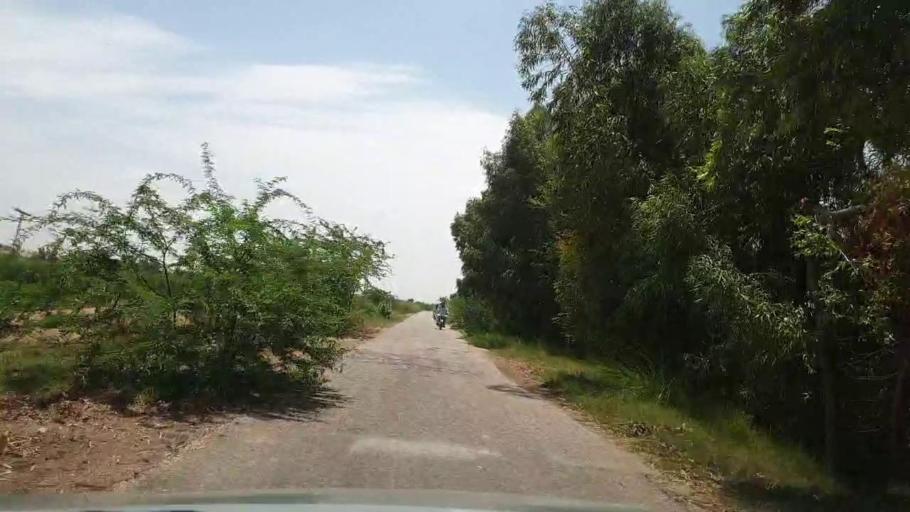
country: PK
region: Sindh
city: Bozdar
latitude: 27.0683
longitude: 68.9804
